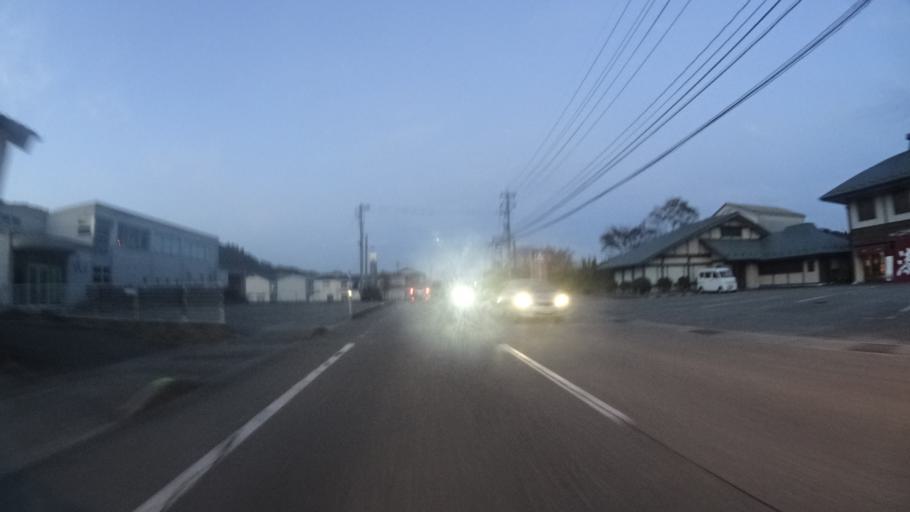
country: JP
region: Ishikawa
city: Nanao
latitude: 37.3820
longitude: 136.8870
